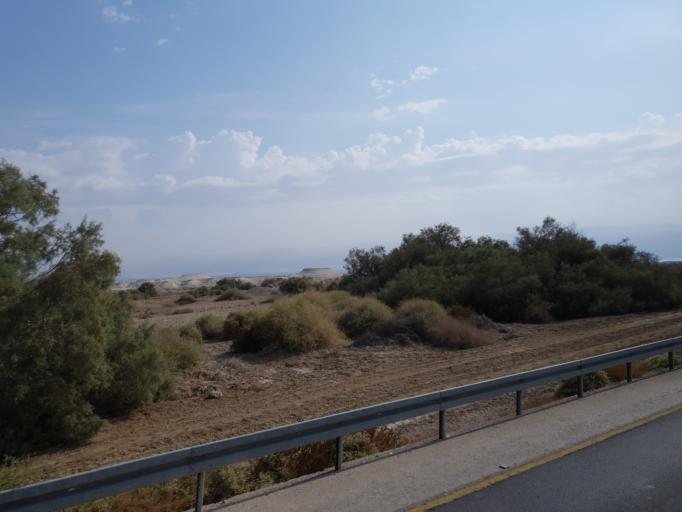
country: PS
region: West Bank
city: Jericho
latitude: 31.7906
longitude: 35.4981
